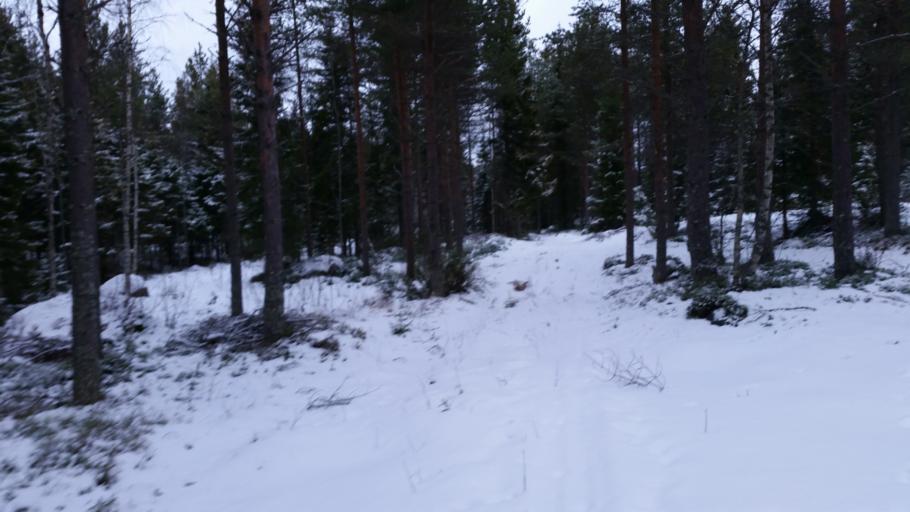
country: SE
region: Vaesterbotten
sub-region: Umea Kommun
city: Saevar
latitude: 63.9153
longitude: 20.7940
